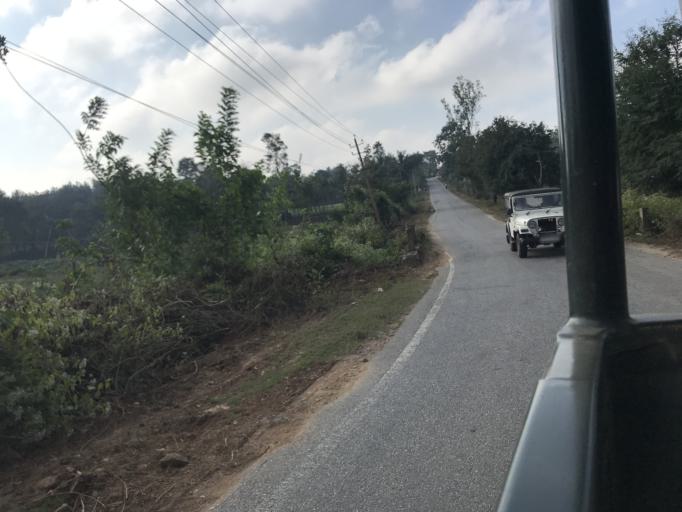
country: IN
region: Karnataka
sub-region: Mysore
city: Heggadadevankote
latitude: 11.9462
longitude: 76.2467
